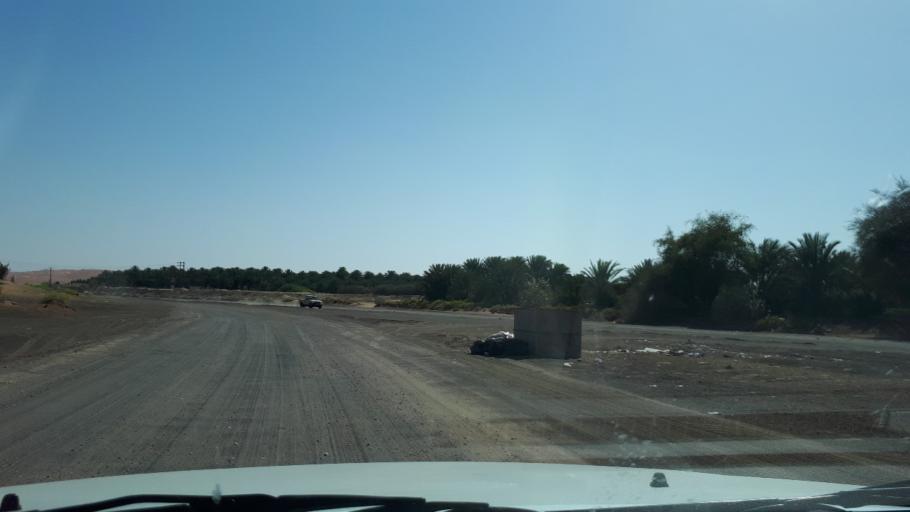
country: OM
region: Ash Sharqiyah
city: Badiyah
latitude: 22.4989
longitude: 58.7509
